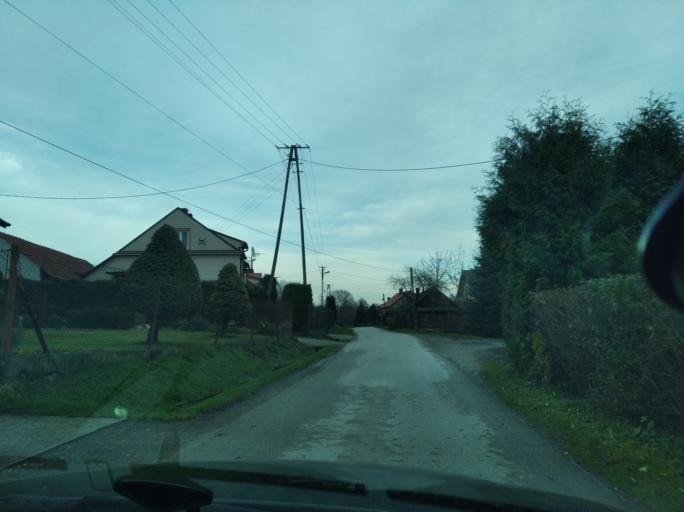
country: PL
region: Subcarpathian Voivodeship
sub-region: Powiat przeworski
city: Debow
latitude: 50.0475
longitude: 22.4438
